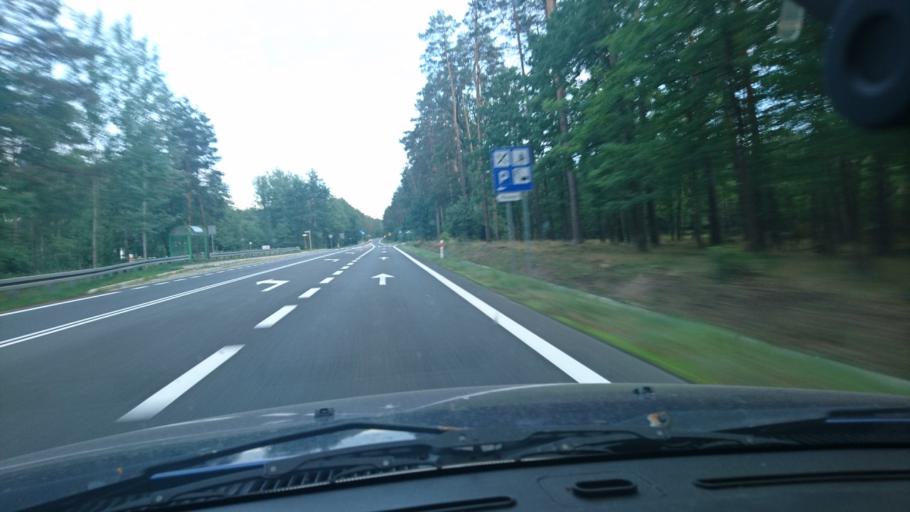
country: PL
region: Silesian Voivodeship
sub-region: Powiat lubliniecki
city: Lubliniec
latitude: 50.6061
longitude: 18.6976
